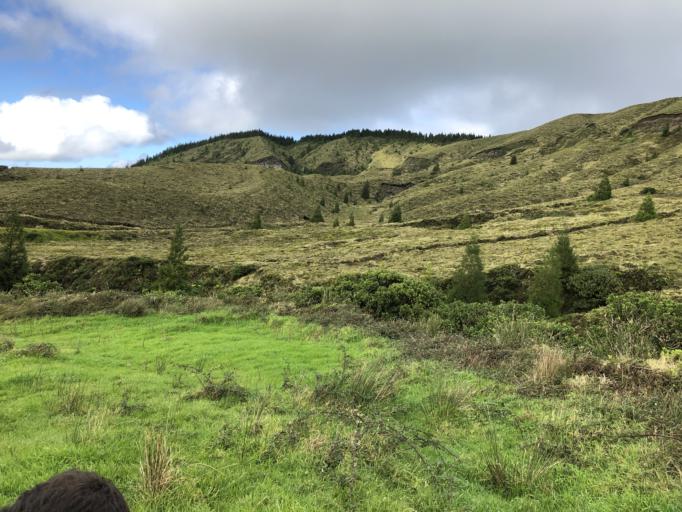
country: PT
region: Azores
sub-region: Ponta Delgada
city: Arrifes
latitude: 37.8330
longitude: -25.7637
